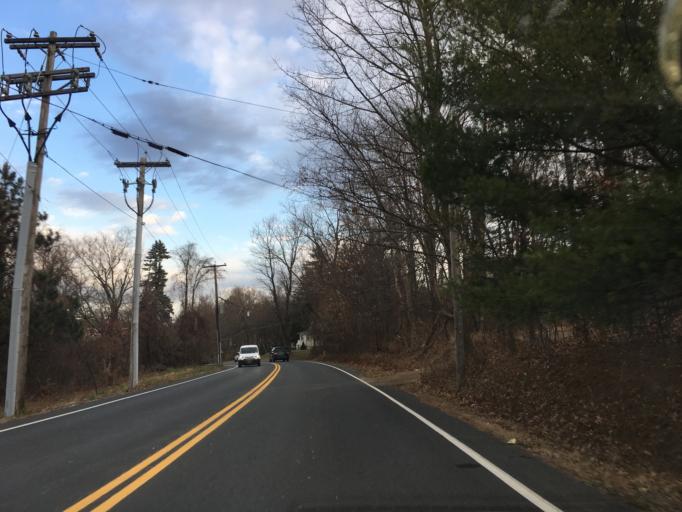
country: US
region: New York
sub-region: Albany County
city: Menands
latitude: 42.6723
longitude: -73.6858
